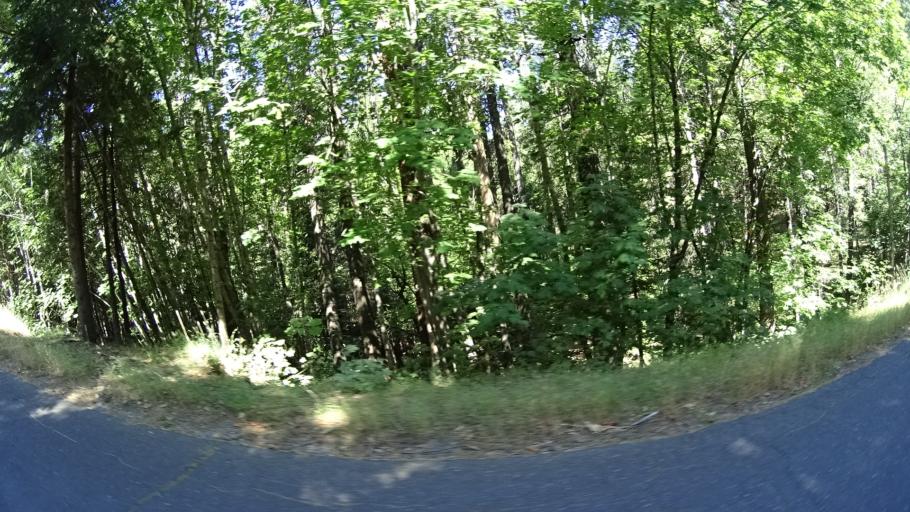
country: US
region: California
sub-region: Calaveras County
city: Arnold
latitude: 38.2400
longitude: -120.3287
